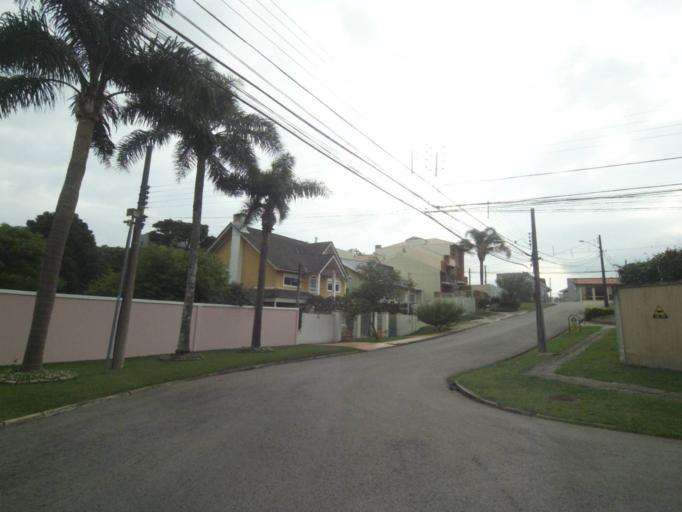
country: BR
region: Parana
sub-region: Curitiba
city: Curitiba
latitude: -25.4098
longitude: -49.3112
